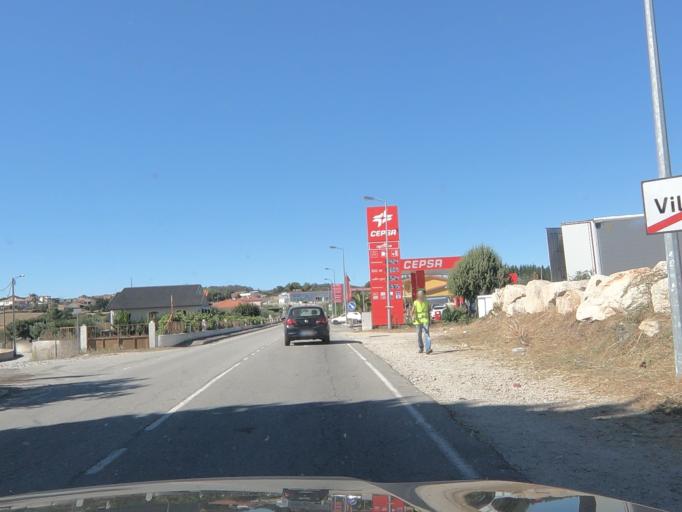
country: PT
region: Vila Real
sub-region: Valpacos
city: Valpacos
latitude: 41.6683
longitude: -7.3364
